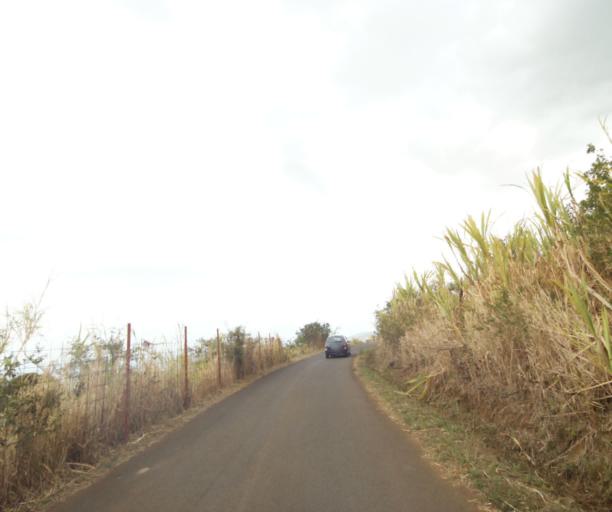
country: RE
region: Reunion
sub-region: Reunion
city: Saint-Paul
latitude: -21.0267
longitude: 55.3013
